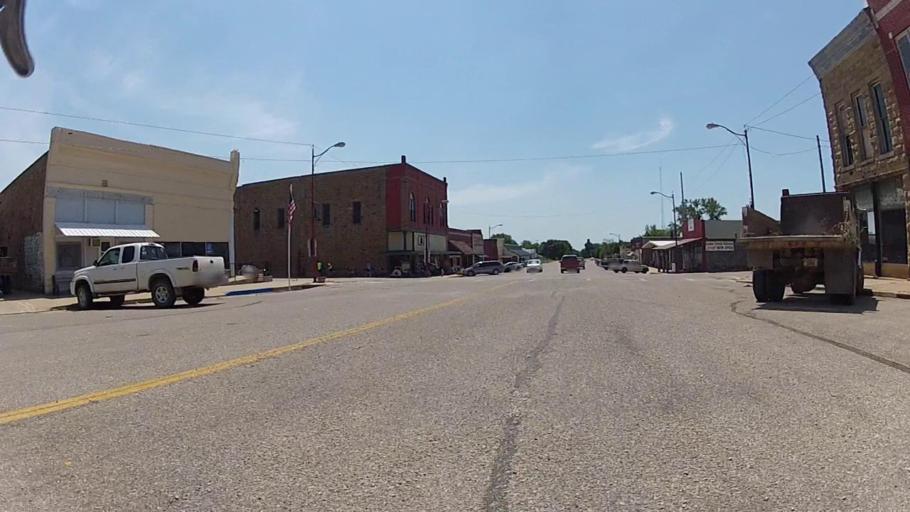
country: US
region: Kansas
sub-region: Chautauqua County
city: Sedan
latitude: 37.1056
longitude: -96.4992
